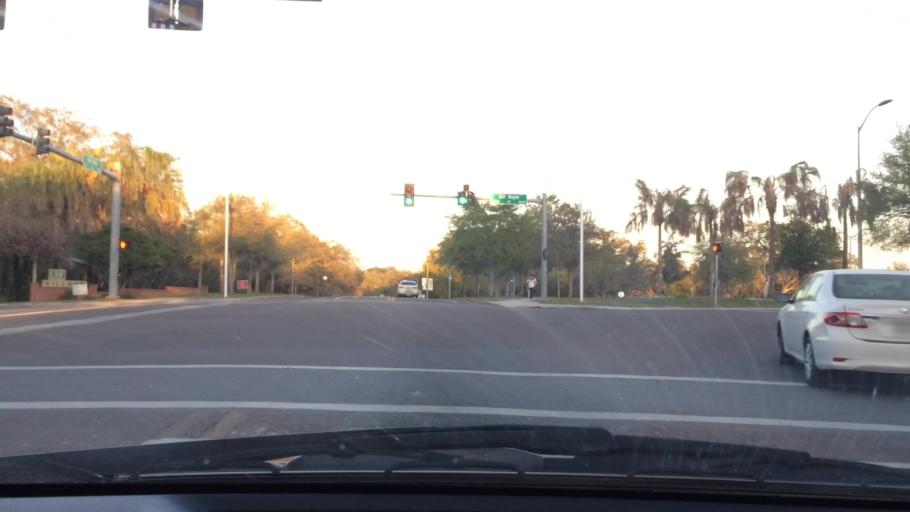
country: US
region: Florida
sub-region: Hillsborough County
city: University
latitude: 28.0657
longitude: -82.4084
